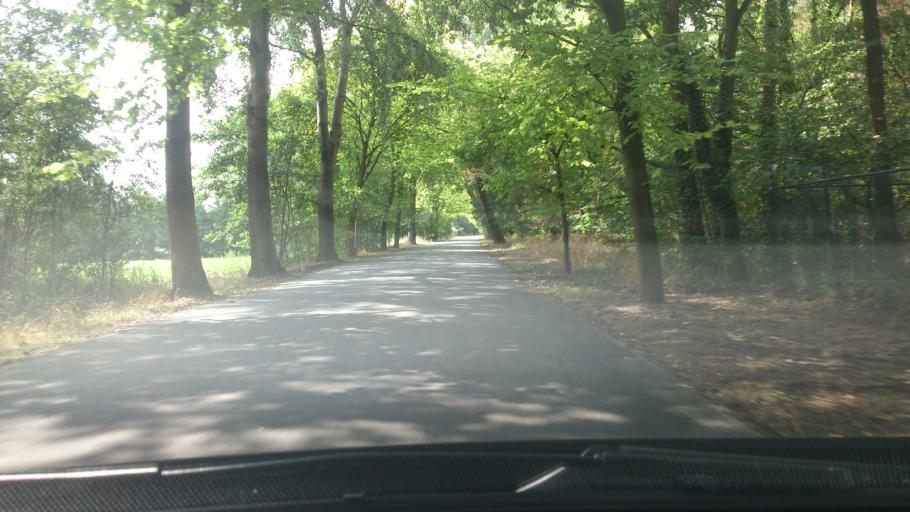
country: BE
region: Flanders
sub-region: Provincie Antwerpen
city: Mol
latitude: 51.2126
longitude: 5.1032
